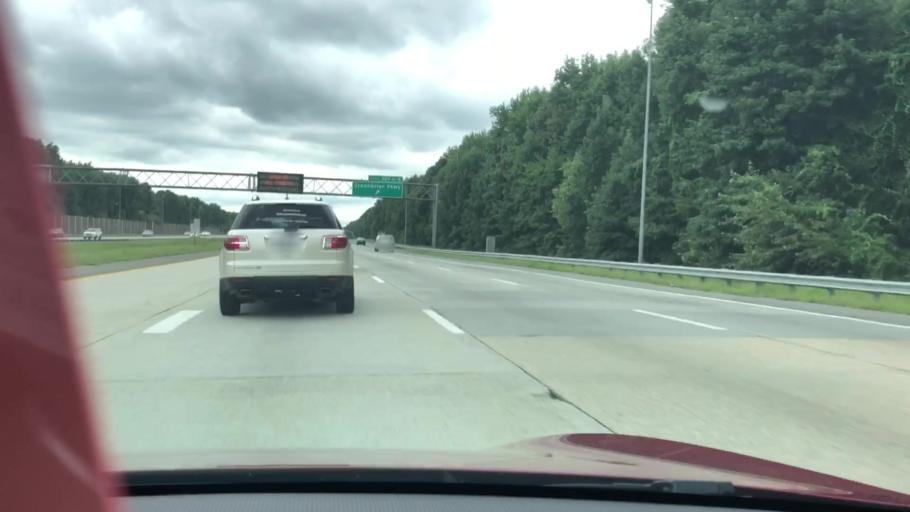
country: US
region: Virginia
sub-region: City of Chesapeake
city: Chesapeake
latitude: 36.7908
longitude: -76.2216
